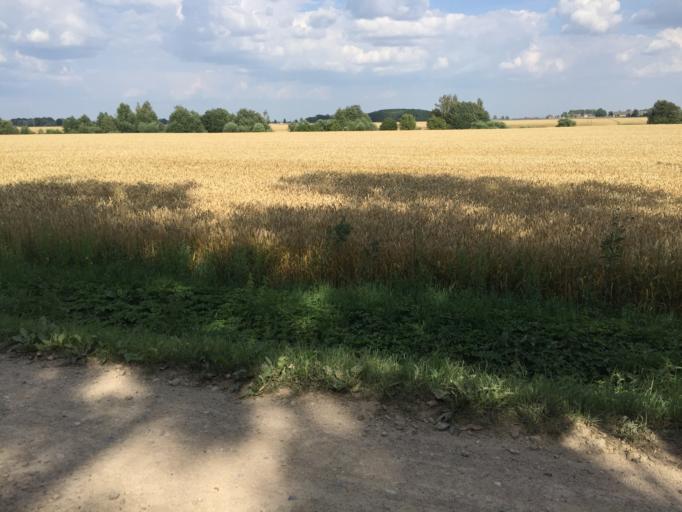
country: LV
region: Jelgava
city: Jelgava
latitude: 56.4817
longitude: 23.7591
